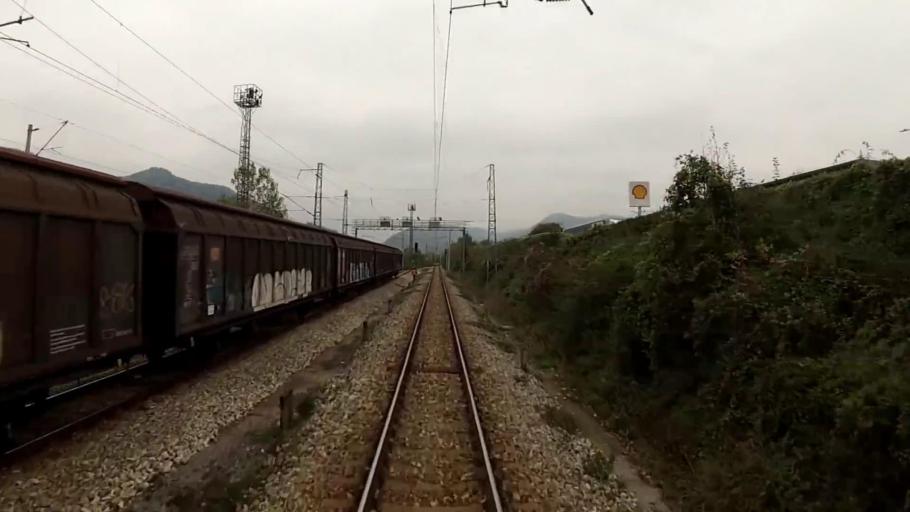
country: RS
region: Central Serbia
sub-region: Pirotski Okrug
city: Dimitrovgrad
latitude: 42.9904
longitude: 22.8516
